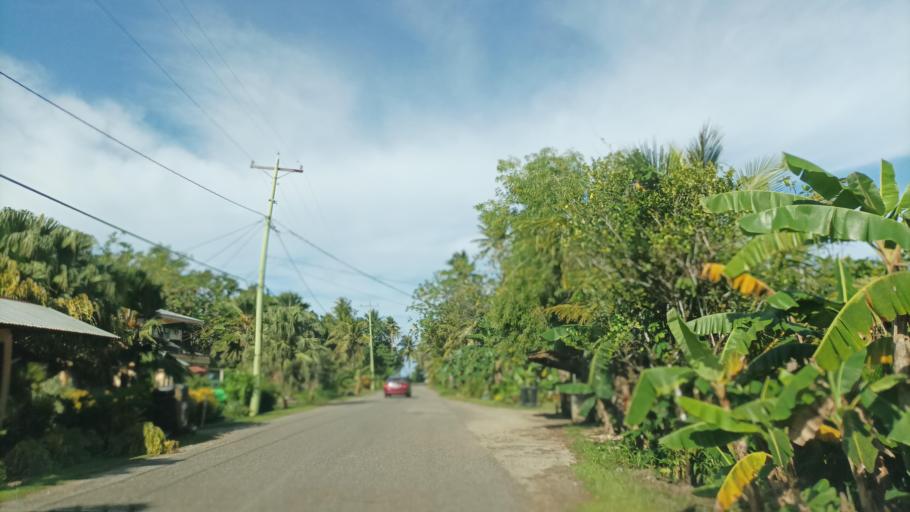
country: FM
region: Kosrae
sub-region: Lelu Municipality
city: Lelu
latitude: 5.3206
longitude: 163.0277
